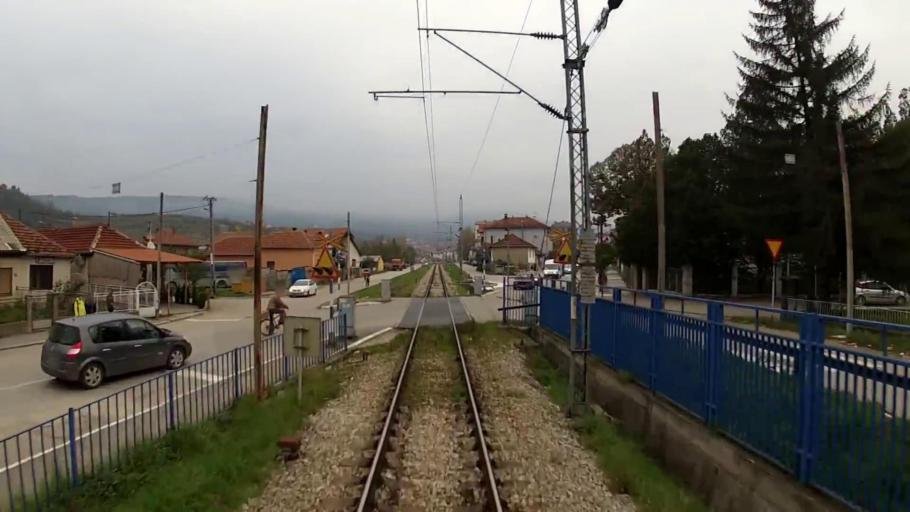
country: RS
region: Central Serbia
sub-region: Pirotski Okrug
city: Dimitrovgrad
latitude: 43.0162
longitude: 22.7830
